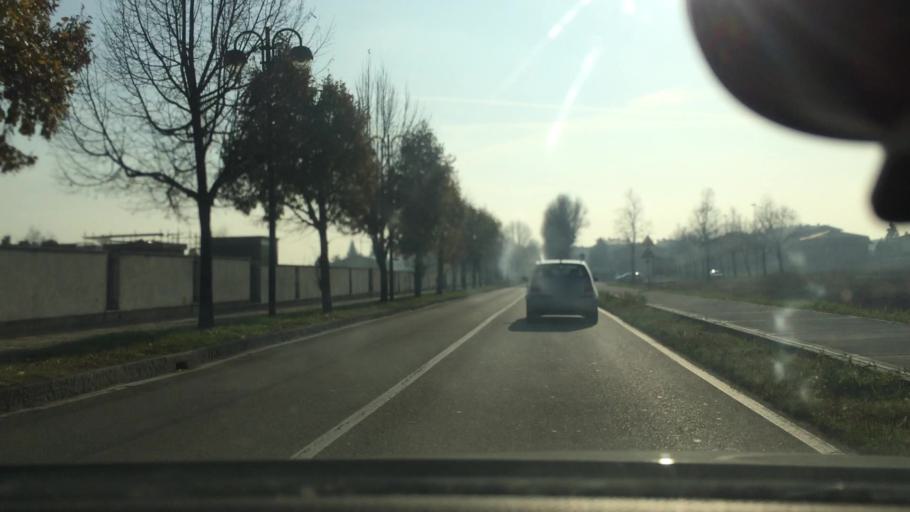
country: IT
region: Lombardy
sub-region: Provincia di Monza e Brianza
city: Ceriano Laghetto
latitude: 45.6217
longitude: 9.0806
